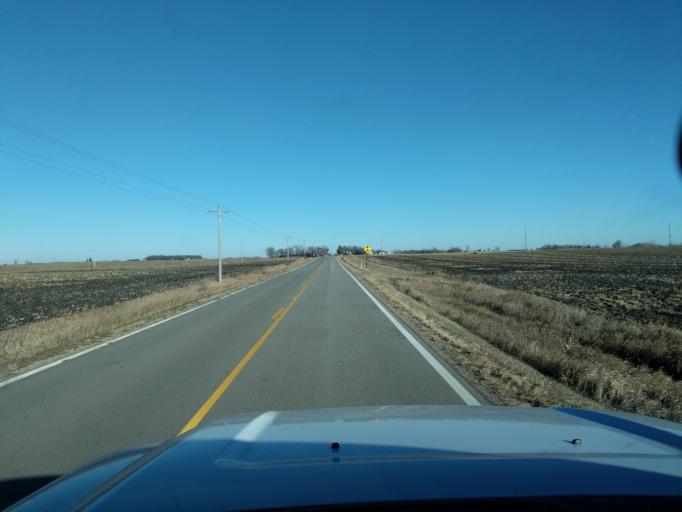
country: US
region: Minnesota
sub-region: Yellow Medicine County
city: Granite Falls
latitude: 44.7859
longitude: -95.4017
